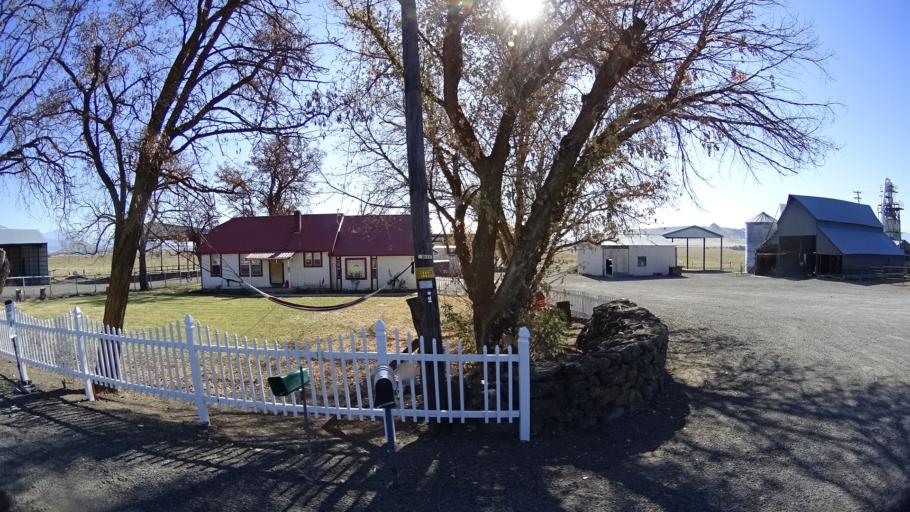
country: US
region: California
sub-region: Siskiyou County
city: Montague
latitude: 41.7237
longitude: -122.4405
